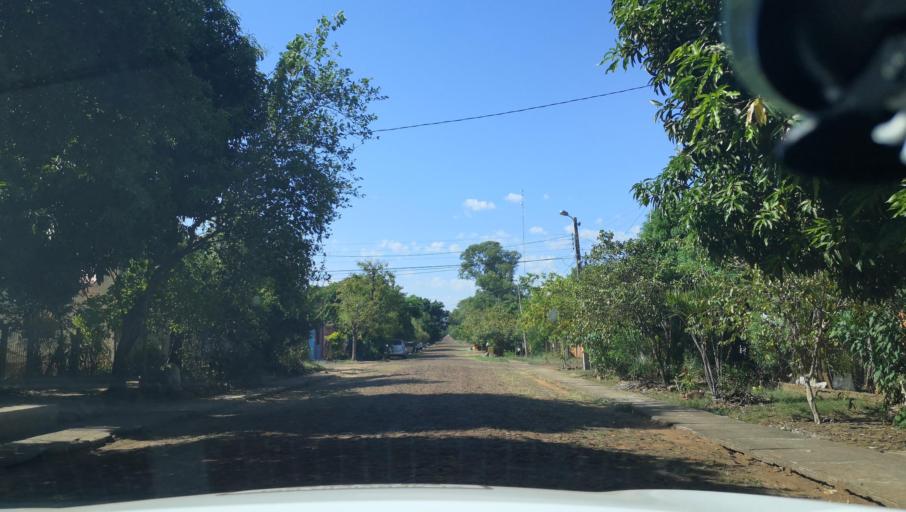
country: PY
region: Itapua
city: Carmen del Parana
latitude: -27.1574
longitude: -56.2357
